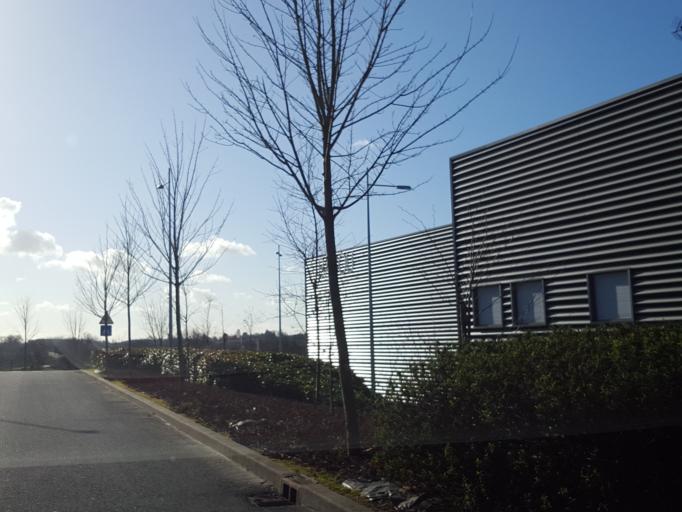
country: FR
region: Pays de la Loire
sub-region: Departement de la Vendee
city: La Roche-sur-Yon
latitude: 46.6409
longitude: -1.4354
